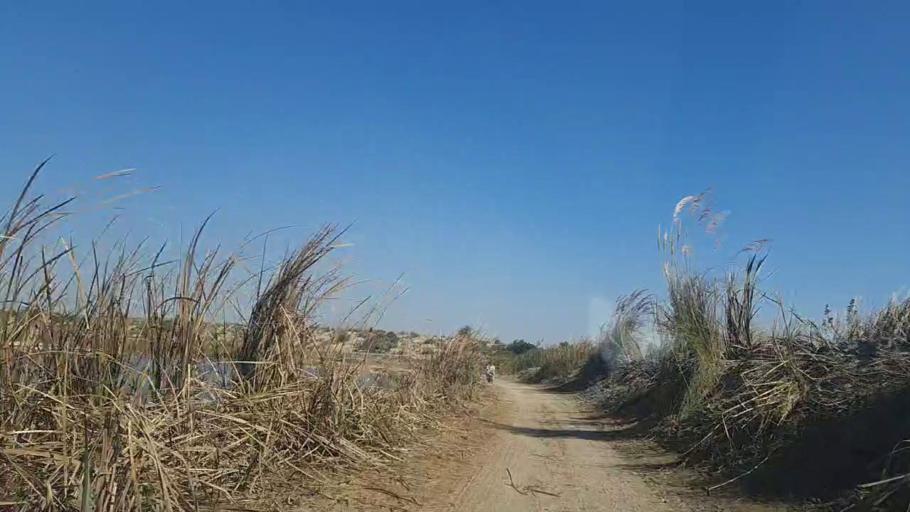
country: PK
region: Sindh
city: Sanghar
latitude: 26.2092
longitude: 68.9277
